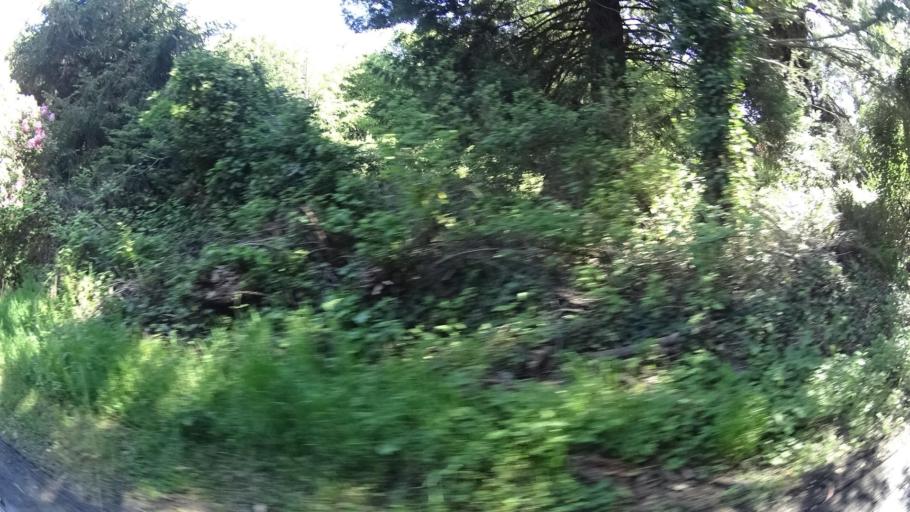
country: US
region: California
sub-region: Humboldt County
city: Rio Dell
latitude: 40.5288
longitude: -124.1669
